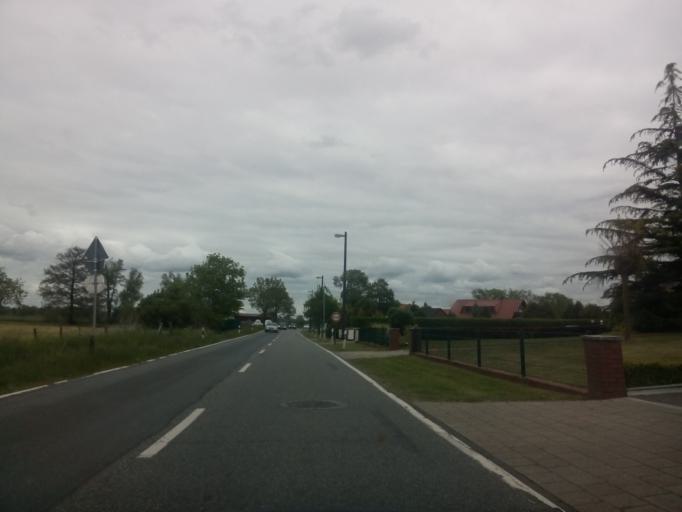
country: DE
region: Lower Saxony
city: Delmenhorst
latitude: 53.0866
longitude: 8.6859
